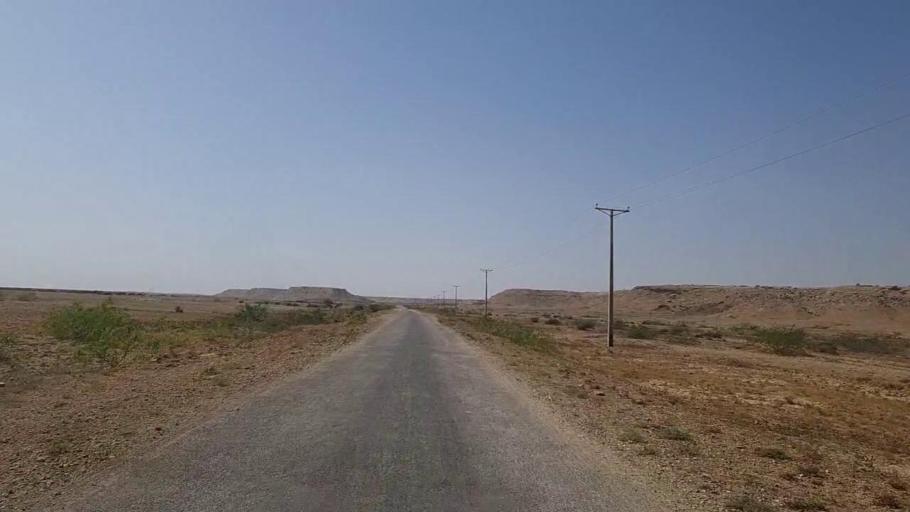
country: PK
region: Sindh
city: Kotri
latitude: 25.1549
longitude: 68.2316
